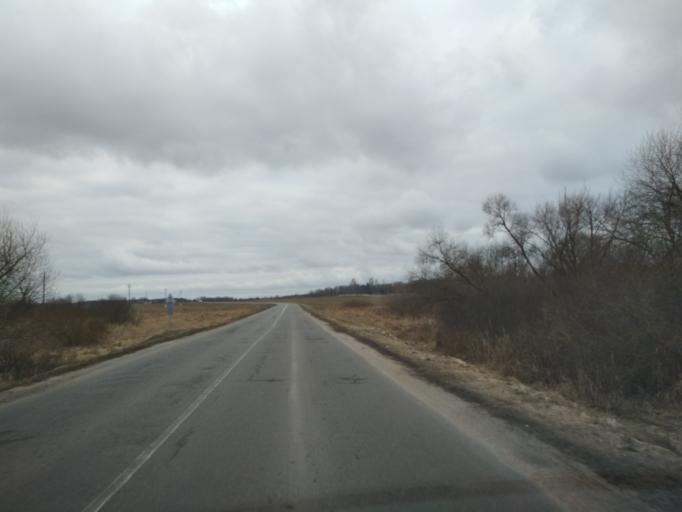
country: BY
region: Minsk
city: Druzhny
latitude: 53.5872
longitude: 27.9003
